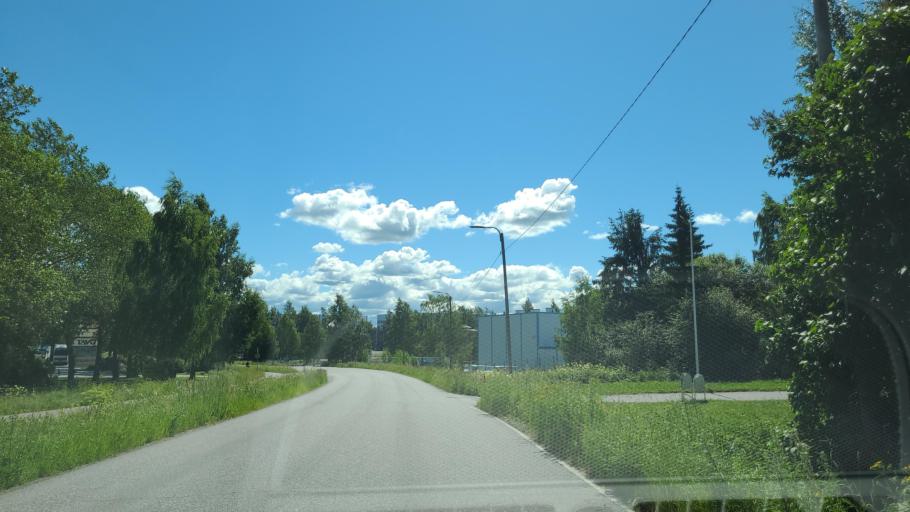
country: FI
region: Ostrobothnia
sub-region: Vaasa
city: Ristinummi
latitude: 63.0617
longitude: 21.7272
